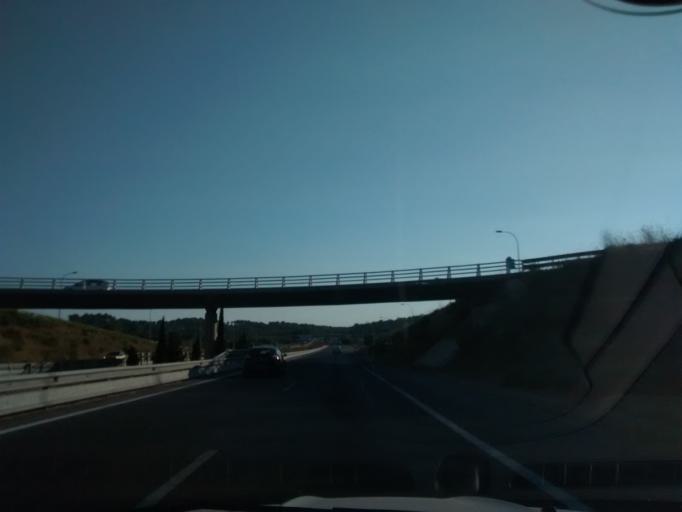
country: ES
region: Balearic Islands
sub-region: Illes Balears
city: Buger
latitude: 39.7808
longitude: 2.9961
